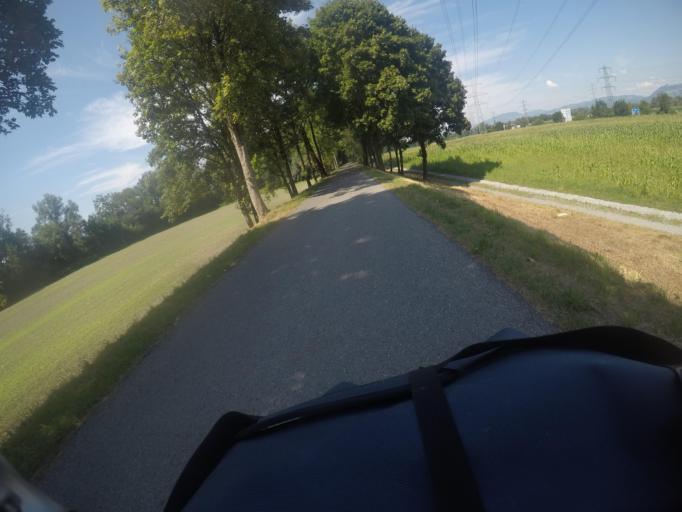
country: AT
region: Vorarlberg
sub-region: Politischer Bezirk Dornbirn
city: Hohenems
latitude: 47.3848
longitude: 9.6764
